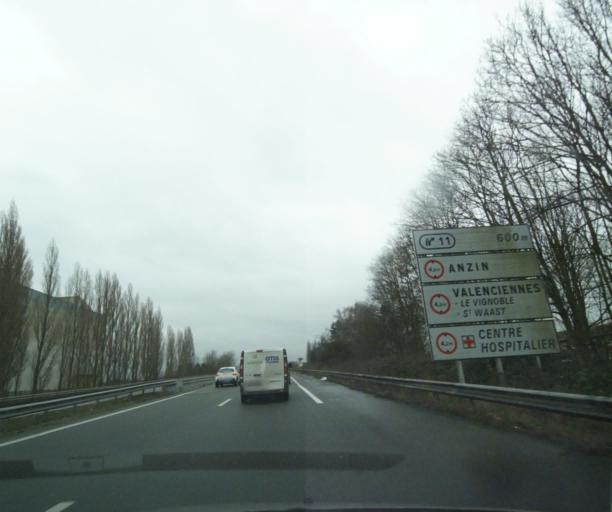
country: FR
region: Nord-Pas-de-Calais
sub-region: Departement du Nord
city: Petite-Foret
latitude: 50.3622
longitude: 3.4851
